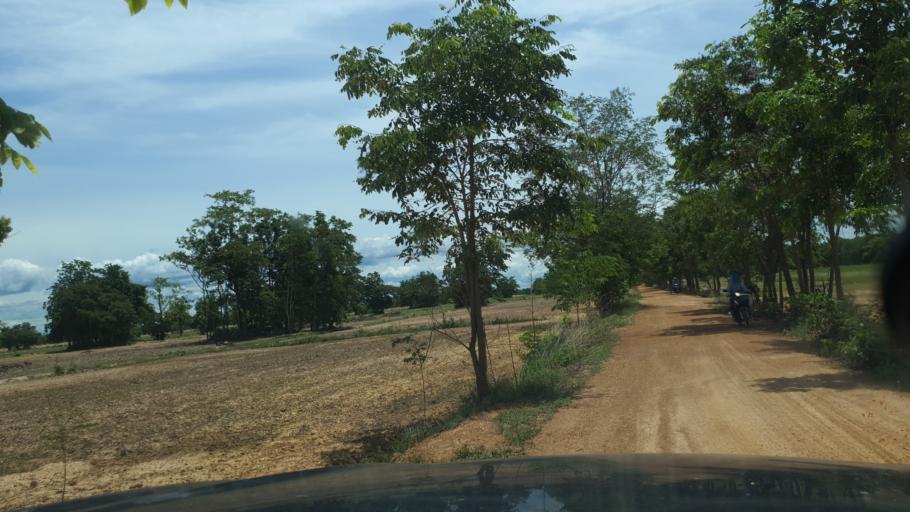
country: TH
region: Sukhothai
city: Ban Na
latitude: 17.1403
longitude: 99.6693
